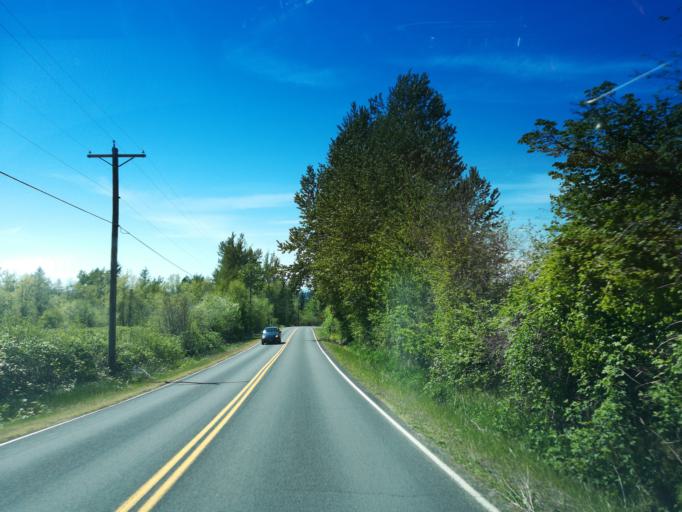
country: US
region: Oregon
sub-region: Multnomah County
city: Troutdale
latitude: 45.5226
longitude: -122.3609
